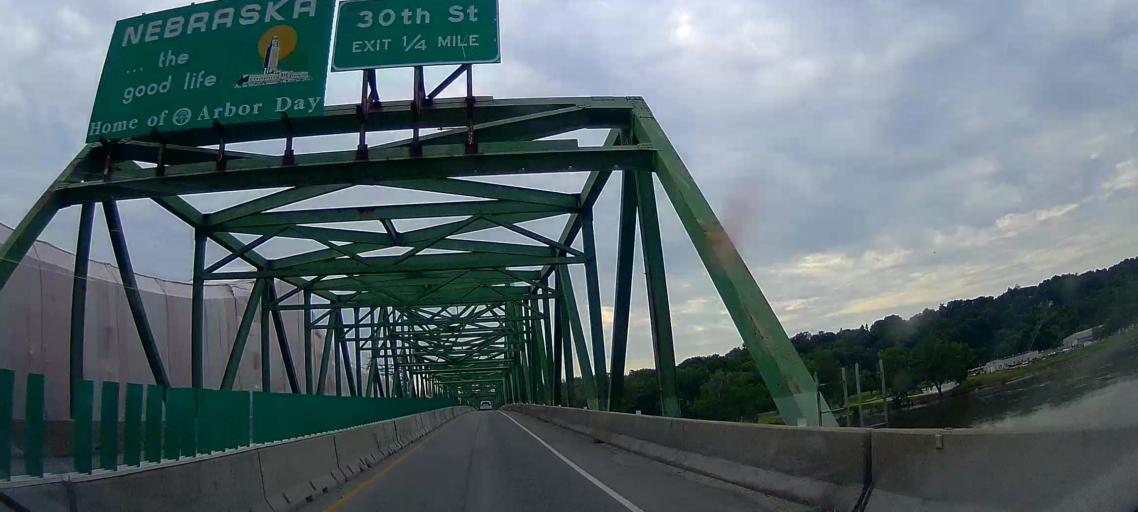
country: US
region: Iowa
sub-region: Pottawattamie County
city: Carter Lake
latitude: 41.3460
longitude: -95.9562
